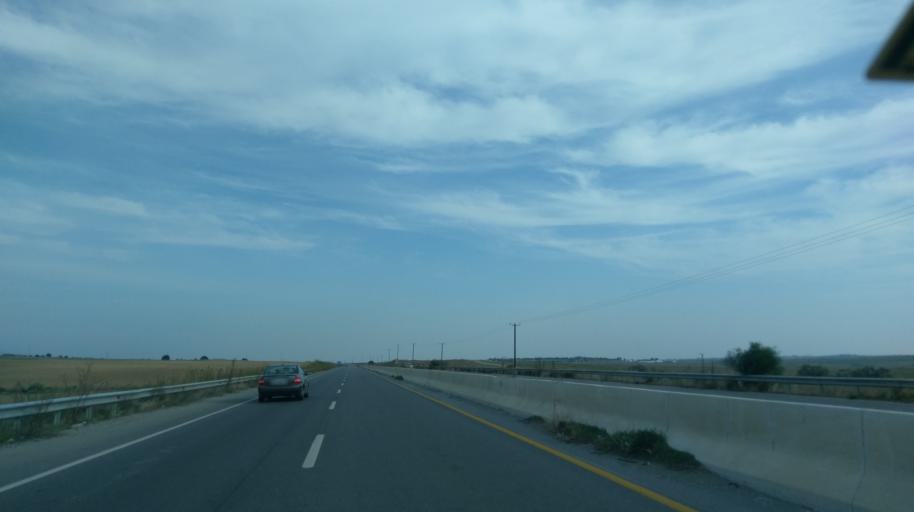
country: CY
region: Lefkosia
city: Mammari
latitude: 35.2118
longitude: 33.2080
